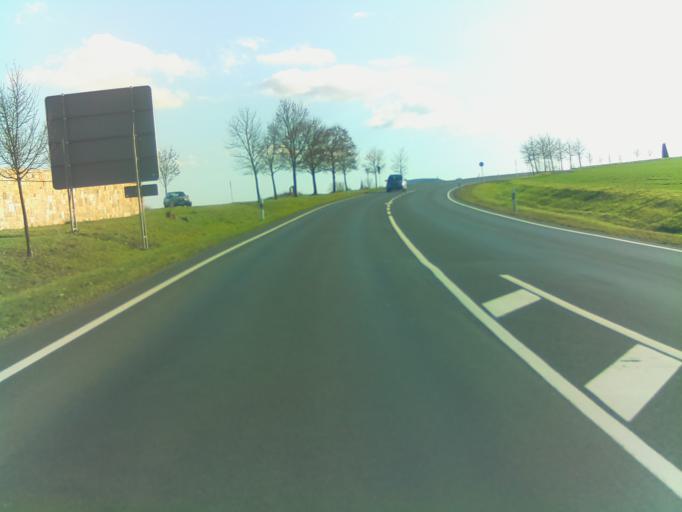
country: DE
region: Bavaria
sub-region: Regierungsbezirk Unterfranken
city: Wuelfershausen
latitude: 50.3277
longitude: 10.3389
